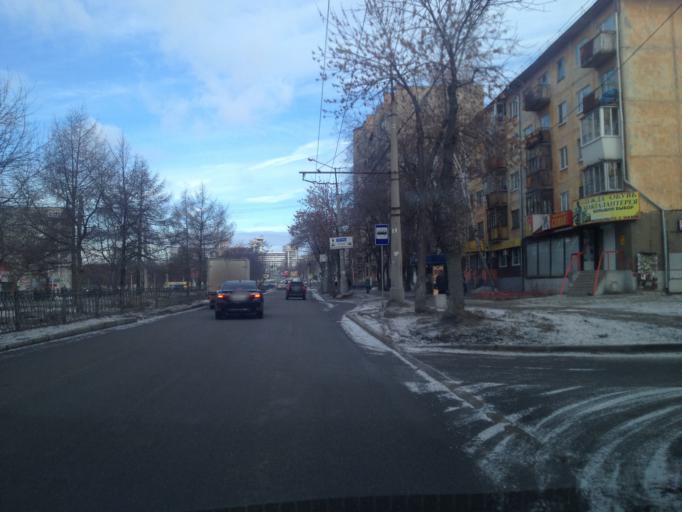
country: RU
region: Sverdlovsk
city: Yekaterinburg
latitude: 56.8220
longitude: 60.5735
